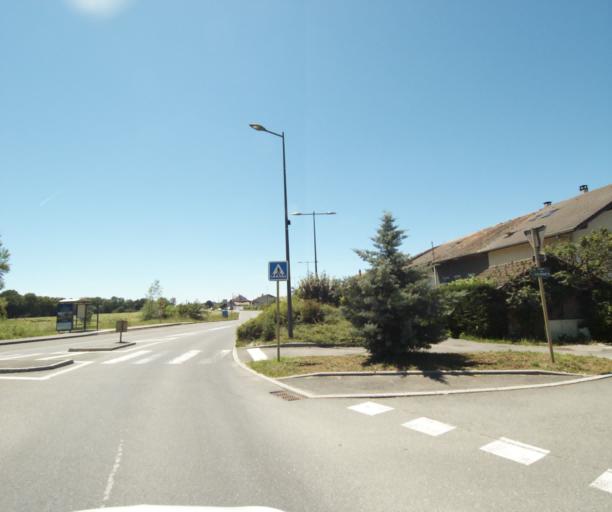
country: FR
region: Rhone-Alpes
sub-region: Departement de la Haute-Savoie
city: Douvaine
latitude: 46.3005
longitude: 6.2838
